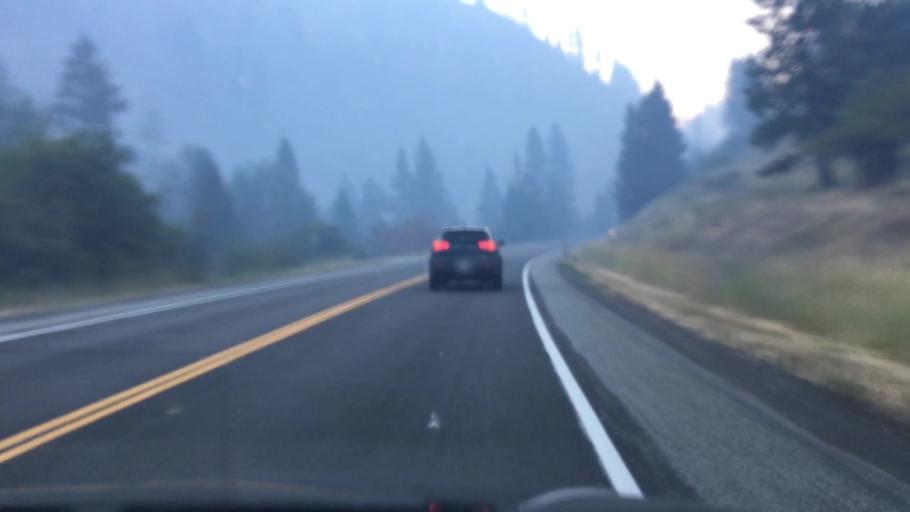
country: US
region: Idaho
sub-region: Valley County
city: McCall
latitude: 45.2716
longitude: -116.3466
